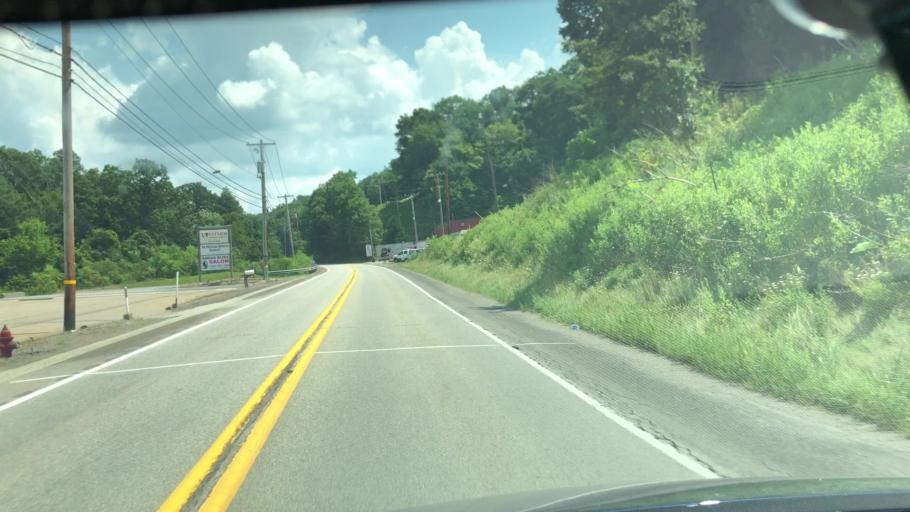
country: US
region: Pennsylvania
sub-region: Armstrong County
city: Freeport
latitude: 40.7128
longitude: -79.7453
